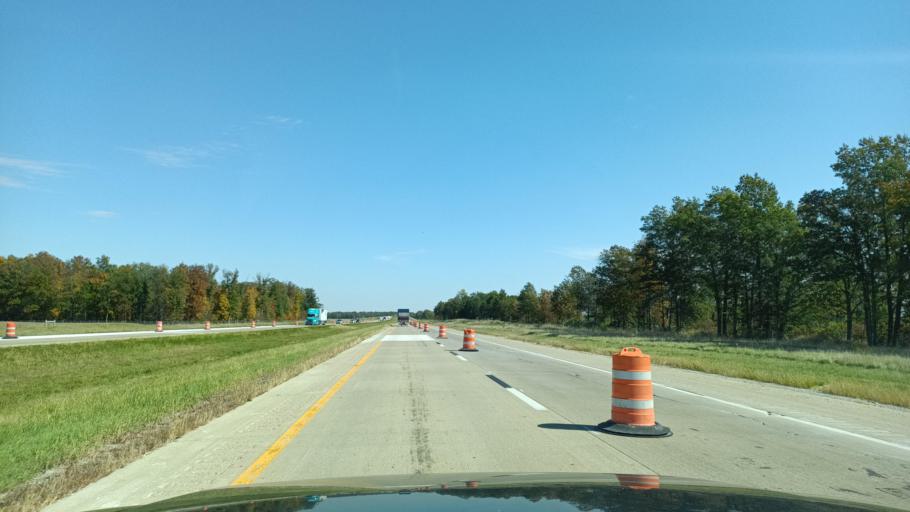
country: US
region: Ohio
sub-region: Defiance County
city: Defiance
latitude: 41.2574
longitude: -84.4537
